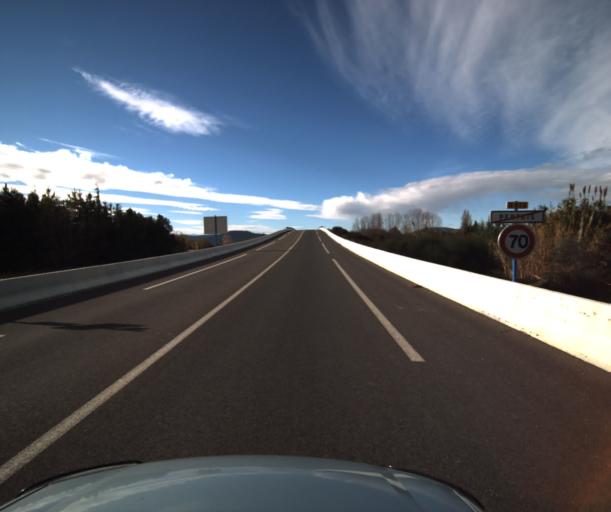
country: FR
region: Provence-Alpes-Cote d'Azur
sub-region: Departement du Vaucluse
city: Pertuis
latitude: 43.6913
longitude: 5.4891
